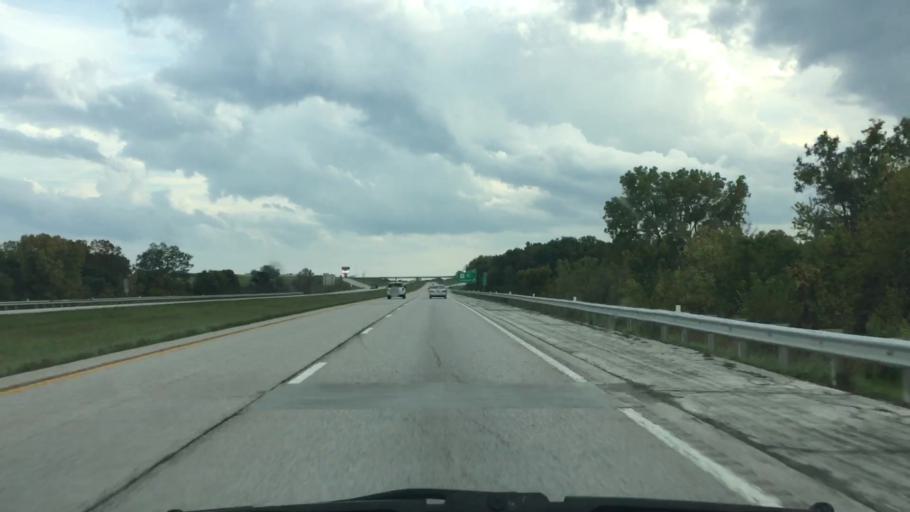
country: US
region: Missouri
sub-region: Clinton County
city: Cameron
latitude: 39.7394
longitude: -94.2205
